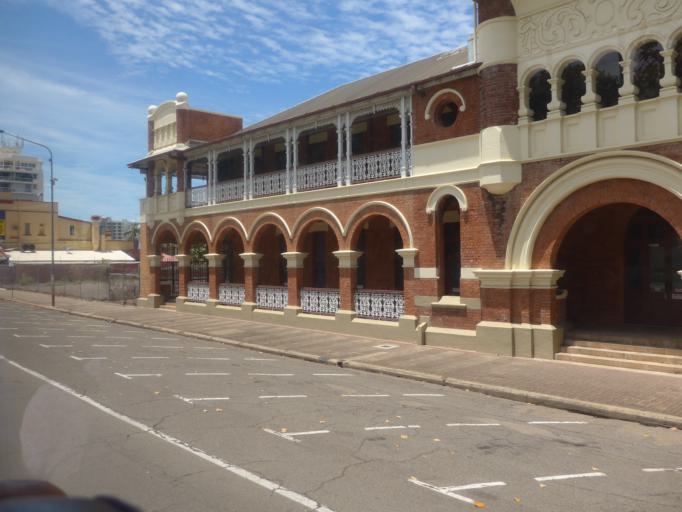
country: AU
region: Queensland
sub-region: Townsville
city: Townsville
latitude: -19.2557
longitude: 146.8228
